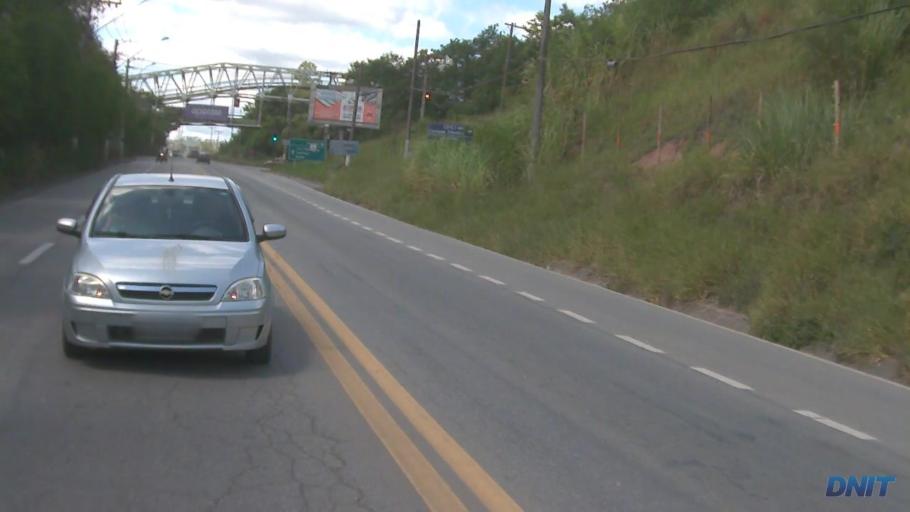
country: BR
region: Minas Gerais
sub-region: Coronel Fabriciano
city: Coronel Fabriciano
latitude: -19.5288
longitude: -42.6525
